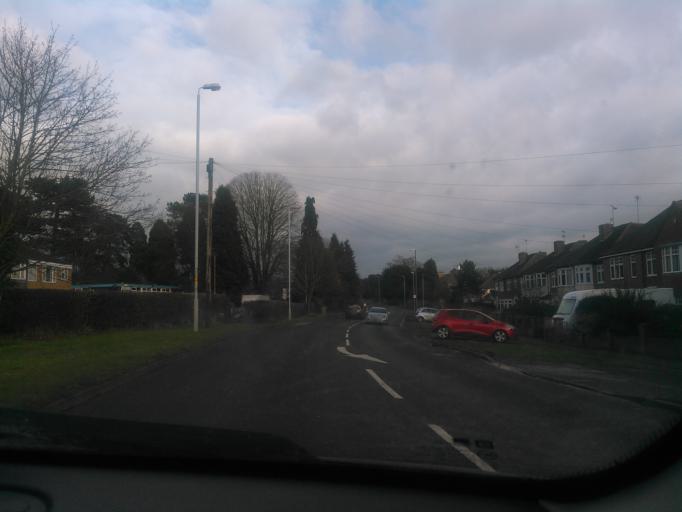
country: GB
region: England
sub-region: Leicestershire
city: Oadby
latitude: 52.5957
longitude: -1.0843
